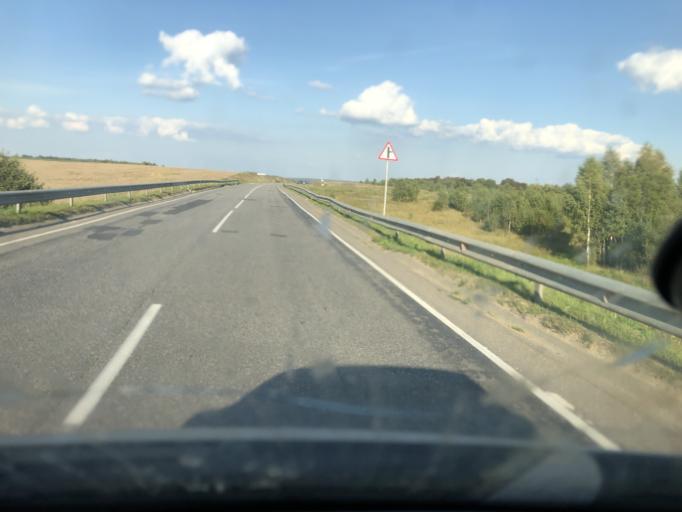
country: RU
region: Kaluga
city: Kozel'sk
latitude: 54.0832
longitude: 35.8197
